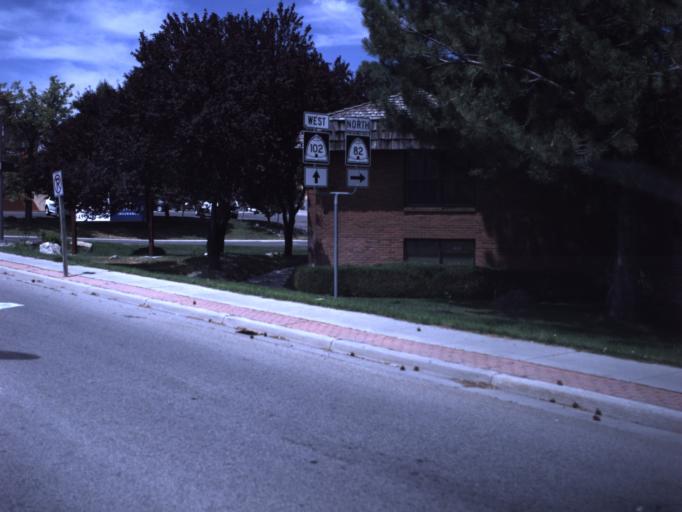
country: US
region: Utah
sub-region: Box Elder County
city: Tremonton
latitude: 41.7119
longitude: -112.1611
